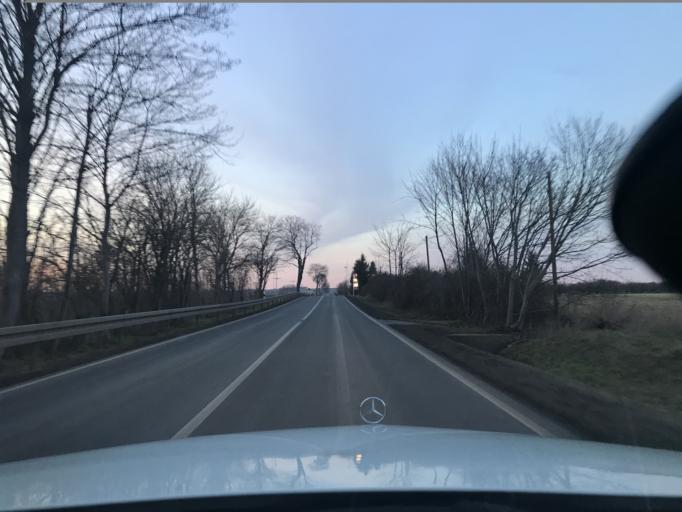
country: DE
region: Thuringia
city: Warza
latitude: 50.9994
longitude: 10.6873
